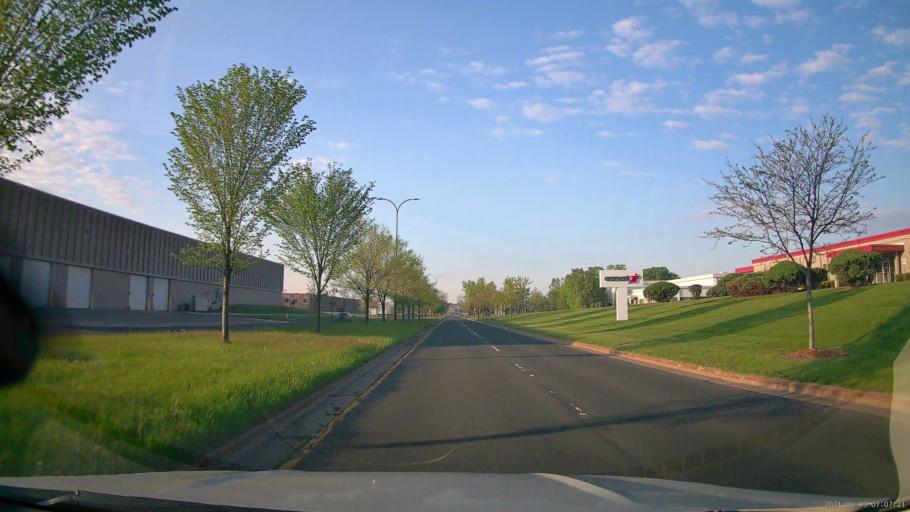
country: US
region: Minnesota
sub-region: Ramsey County
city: Lauderdale
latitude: 44.9979
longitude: -93.2117
